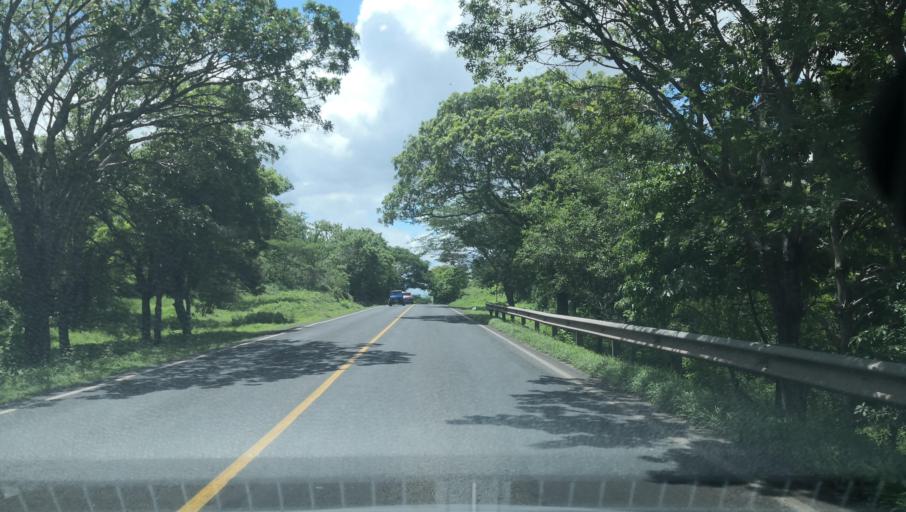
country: NI
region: Esteli
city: Condega
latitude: 13.3900
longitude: -86.4012
